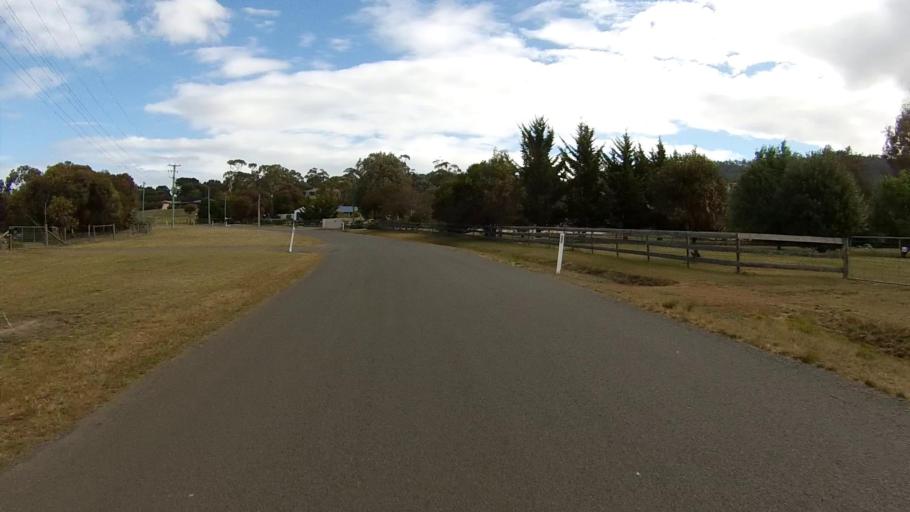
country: AU
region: Tasmania
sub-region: Clarence
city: Seven Mile Beach
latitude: -42.8571
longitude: 147.4827
